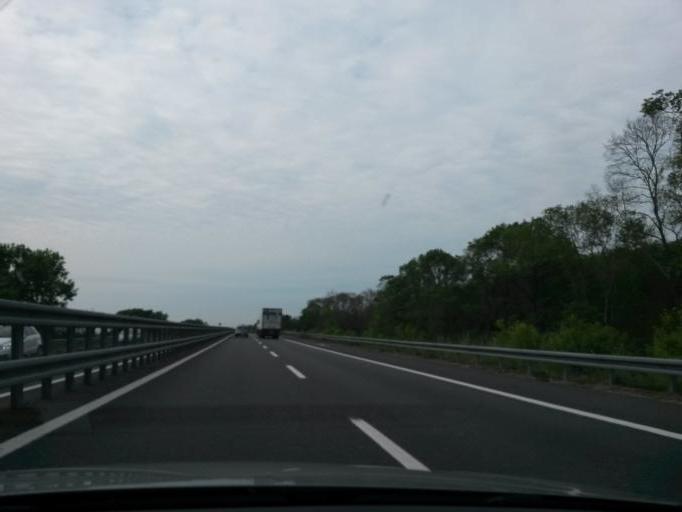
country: IT
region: Tuscany
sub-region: Province of Pisa
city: Madonna dell'Acqua
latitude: 43.7376
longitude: 10.3526
